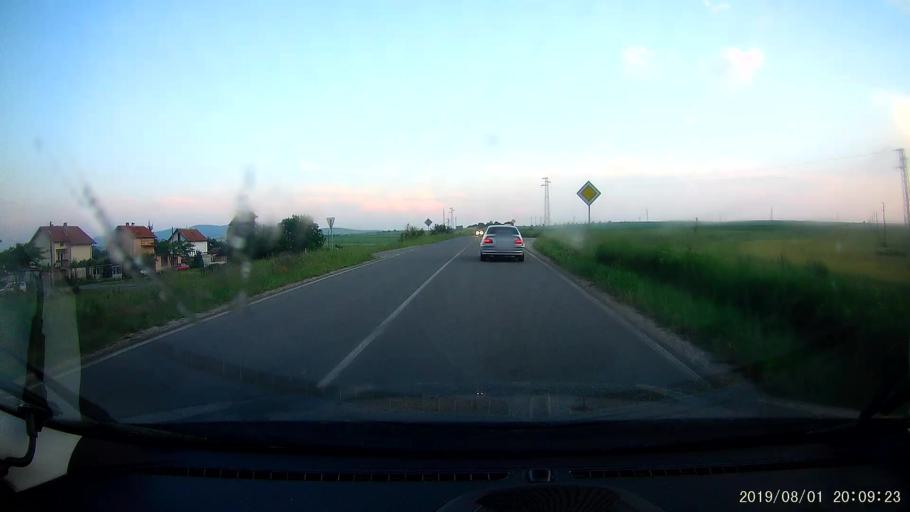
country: BG
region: Yambol
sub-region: Obshtina Yambol
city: Yambol
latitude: 42.4986
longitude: 26.5924
